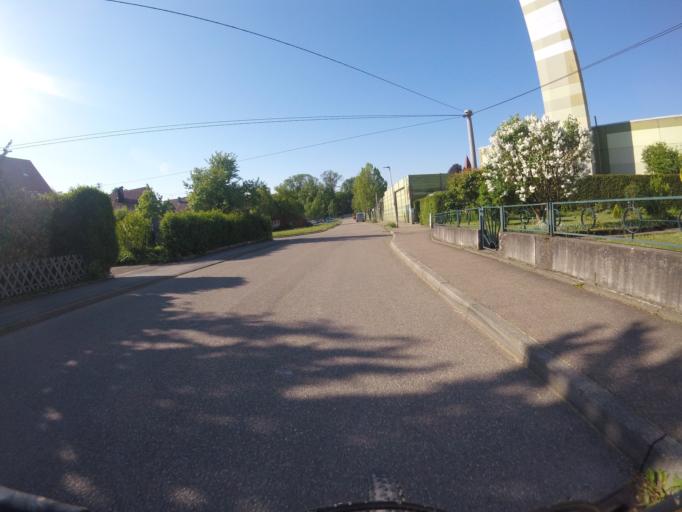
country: DE
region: Baden-Wuerttemberg
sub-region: Regierungsbezirk Stuttgart
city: Aspach
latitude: 48.9913
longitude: 9.4084
